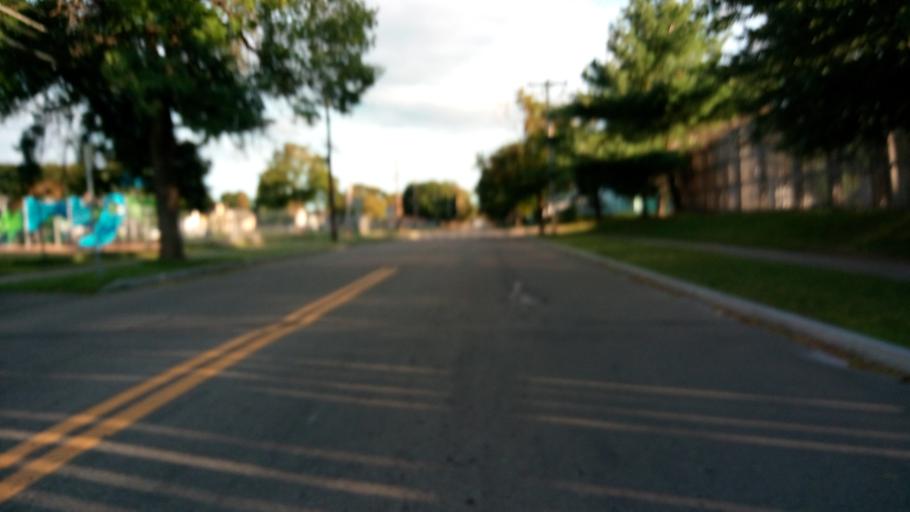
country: US
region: New York
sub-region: Chemung County
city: Elmira
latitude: 42.1061
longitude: -76.8078
